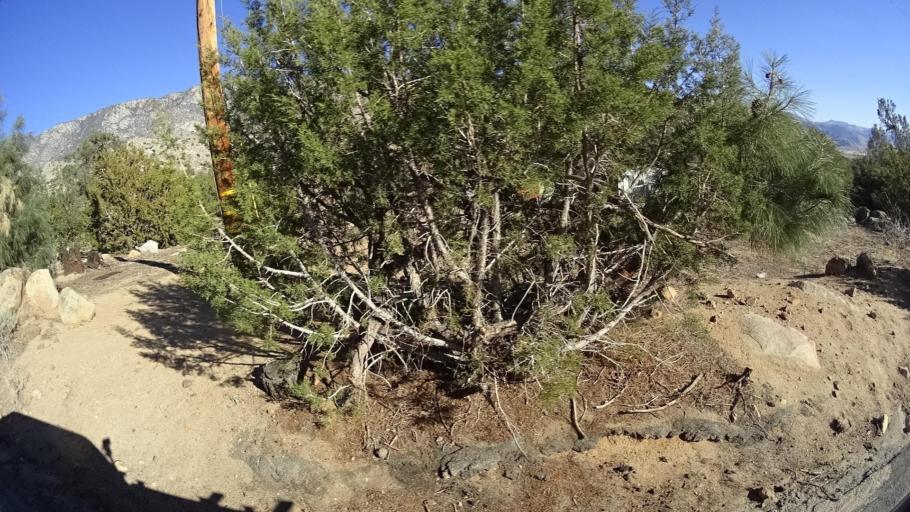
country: US
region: California
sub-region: Kern County
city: Weldon
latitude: 35.7175
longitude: -118.3057
